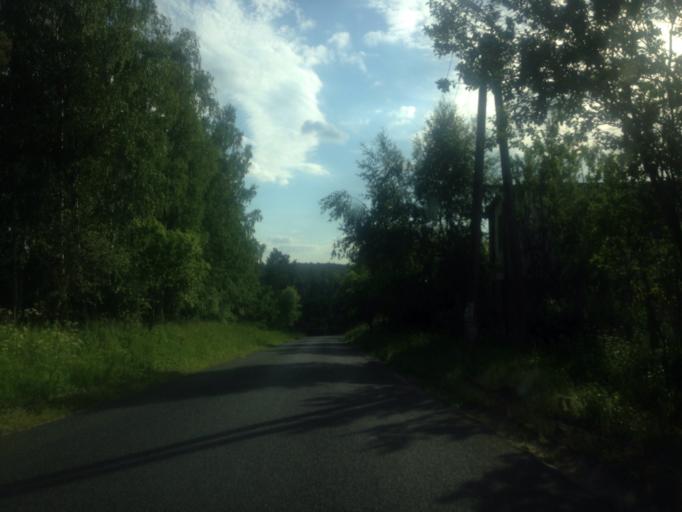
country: PL
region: Kujawsko-Pomorskie
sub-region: Powiat brodnicki
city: Brodnica
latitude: 53.3409
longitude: 19.4330
